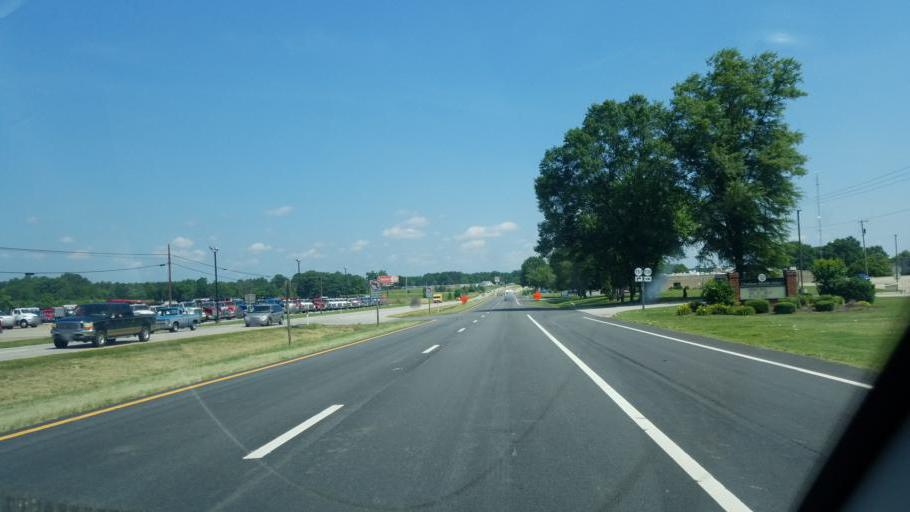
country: US
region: Virginia
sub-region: Pittsylvania County
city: Chatham
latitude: 36.7614
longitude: -79.3894
